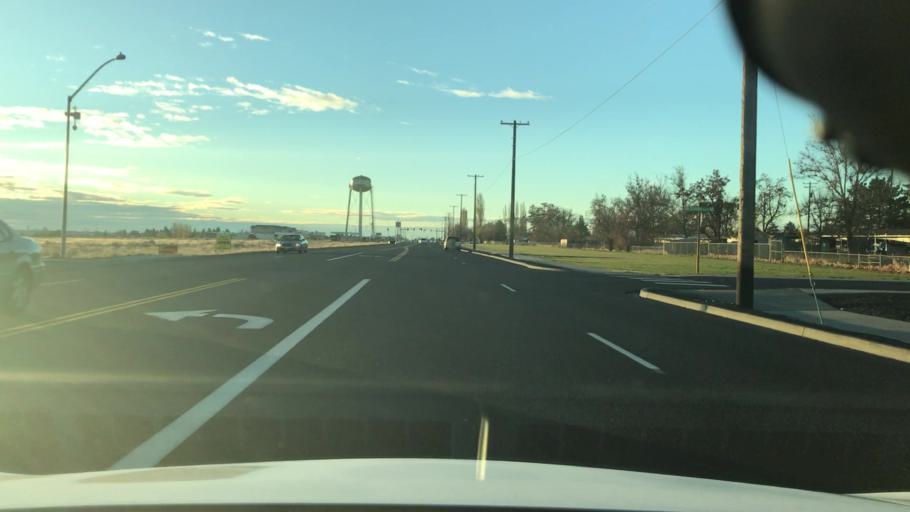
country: US
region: Washington
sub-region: Grant County
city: Moses Lake North
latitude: 47.1675
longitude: -119.3158
